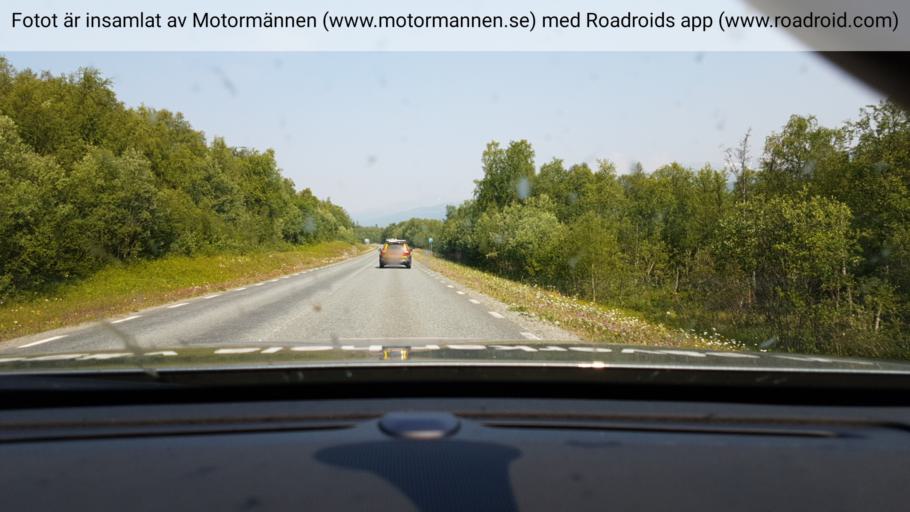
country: NO
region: Nordland
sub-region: Rana
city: Mo i Rana
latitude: 65.7641
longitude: 15.1150
